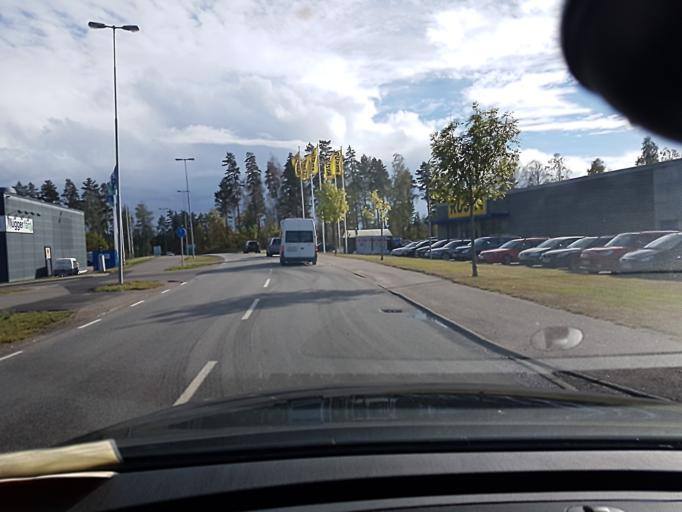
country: SE
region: Kronoberg
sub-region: Vaxjo Kommun
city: Vaexjoe
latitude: 56.8816
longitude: 14.7636
